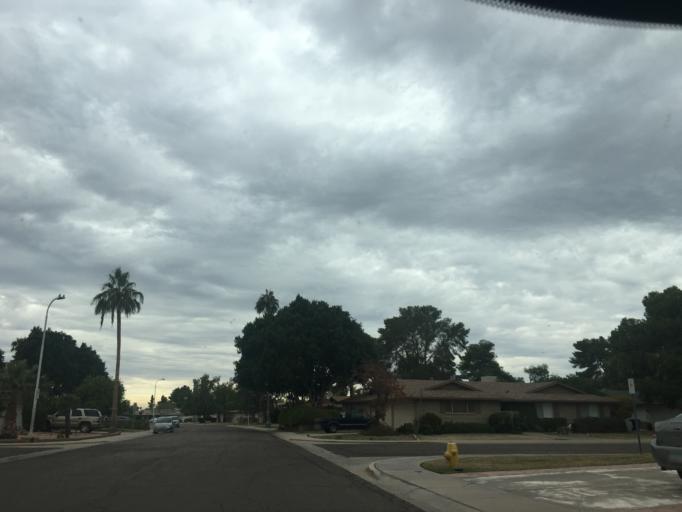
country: US
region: Arizona
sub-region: Maricopa County
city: Guadalupe
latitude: 33.3699
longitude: -111.9222
